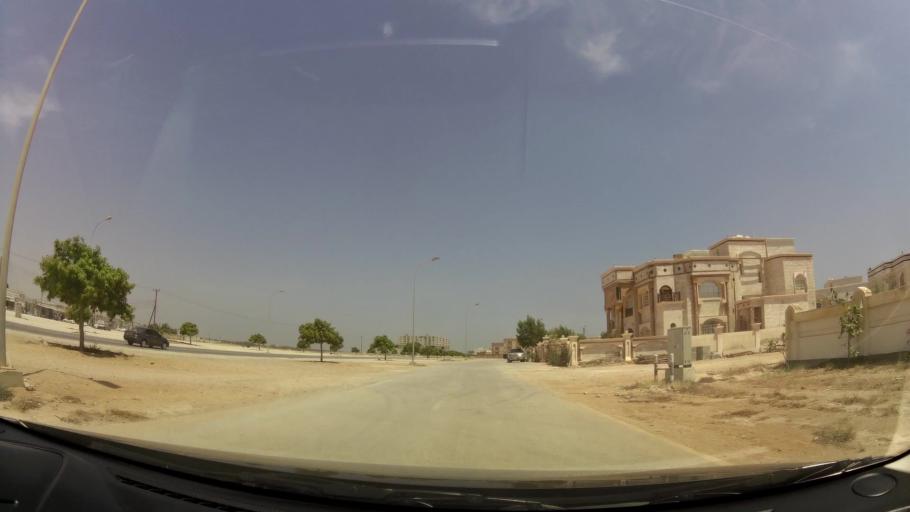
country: OM
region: Zufar
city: Salalah
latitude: 17.0575
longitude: 54.1639
